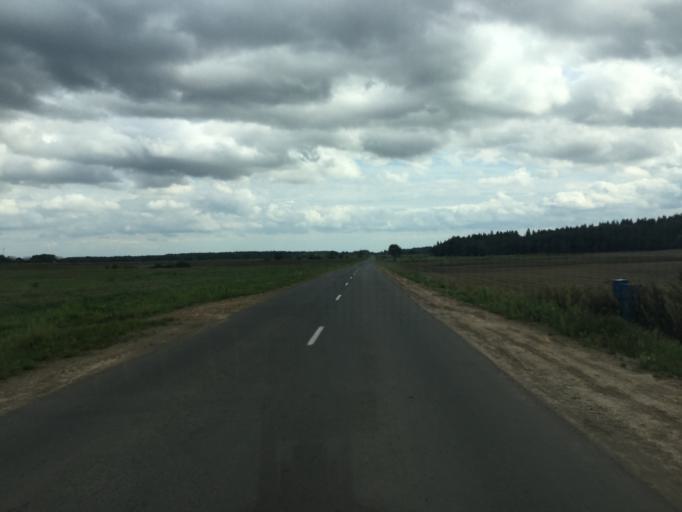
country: BY
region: Vitebsk
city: Vitebsk
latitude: 55.1428
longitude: 30.2879
